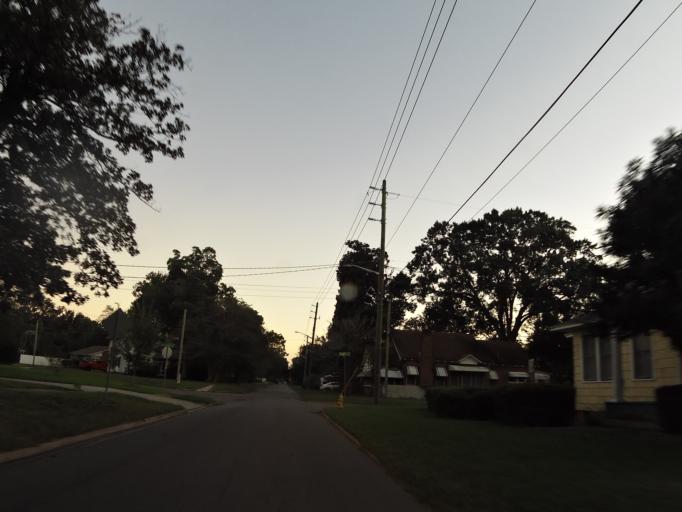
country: US
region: Florida
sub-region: Duval County
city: Jacksonville
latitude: 30.3132
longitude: -81.7222
